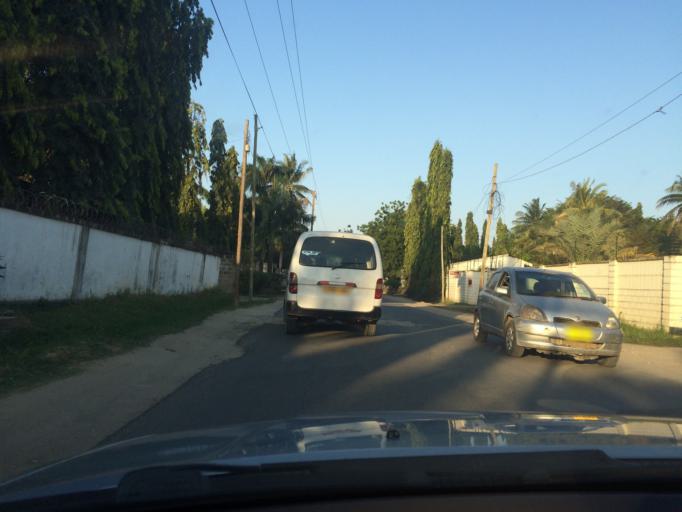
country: TZ
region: Dar es Salaam
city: Magomeni
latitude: -6.7727
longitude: 39.2579
